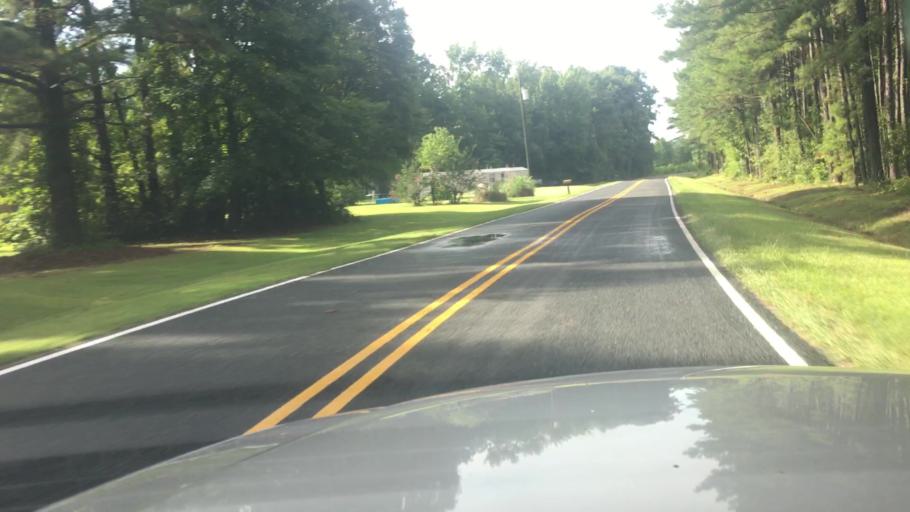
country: US
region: North Carolina
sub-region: Cumberland County
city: Eastover
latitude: 35.1598
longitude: -78.8538
